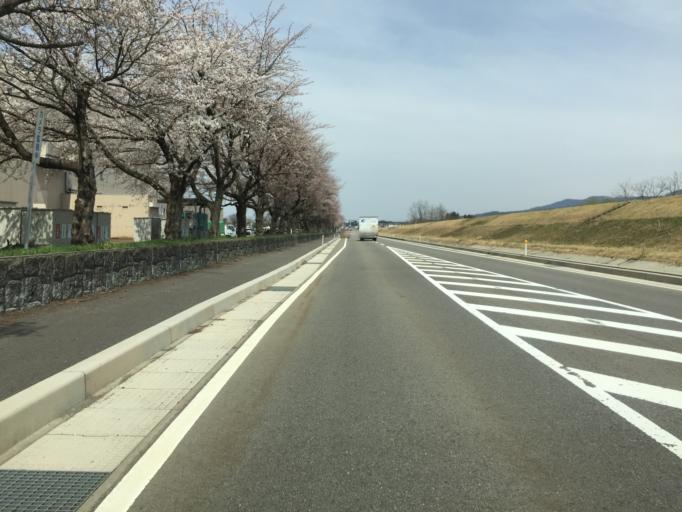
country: JP
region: Niigata
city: Ojiya
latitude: 37.3239
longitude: 138.8079
